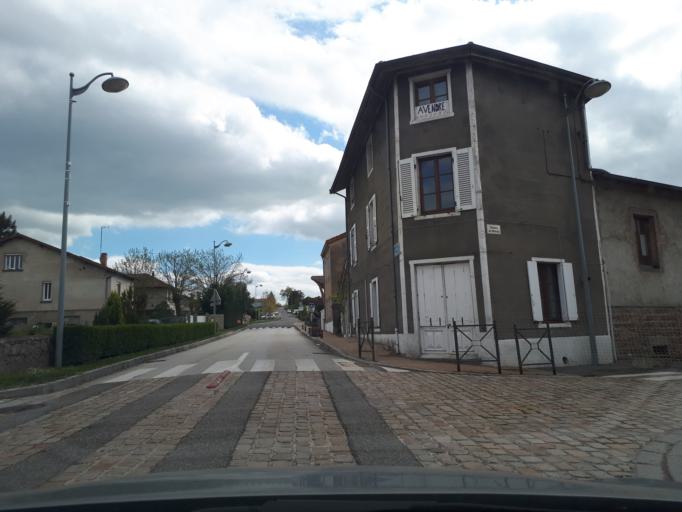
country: FR
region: Rhone-Alpes
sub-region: Departement de la Loire
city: Civens
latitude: 45.7367
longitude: 4.2882
